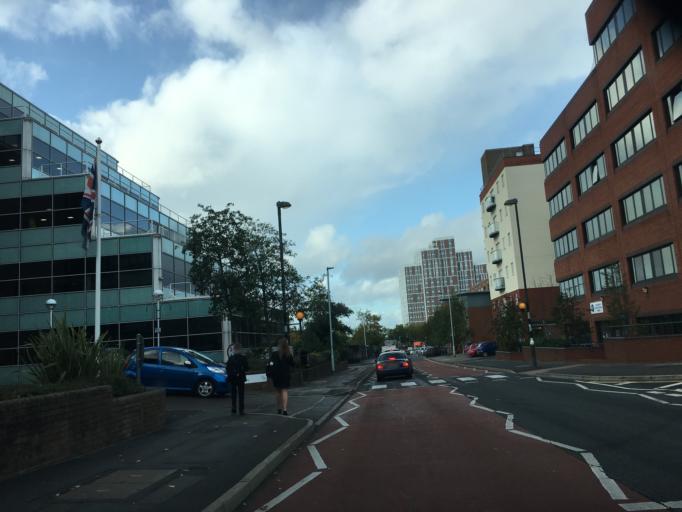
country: GB
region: England
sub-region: Bracknell Forest
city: Bracknell
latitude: 51.4140
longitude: -0.7526
